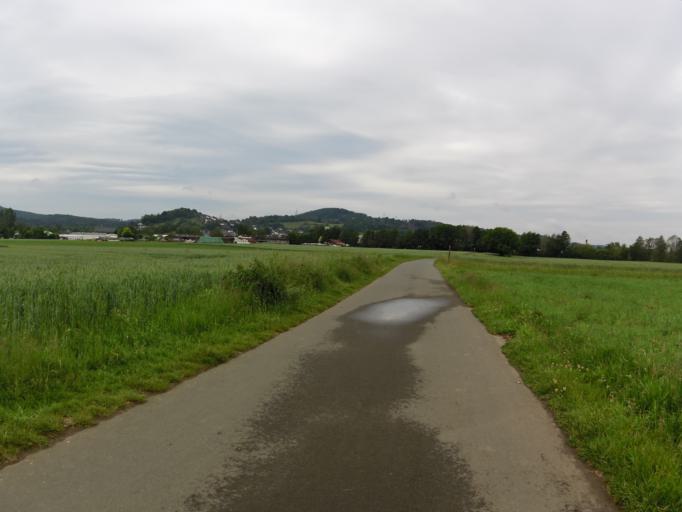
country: DE
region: Hesse
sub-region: Regierungsbezirk Kassel
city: Rotenburg an der Fulda
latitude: 50.9904
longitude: 9.7519
